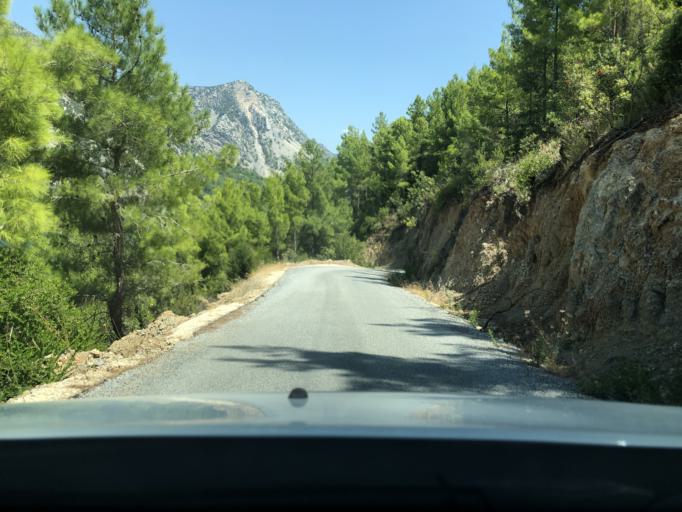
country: TR
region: Antalya
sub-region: Manavgat
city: Manavgat
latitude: 36.9120
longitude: 31.5444
